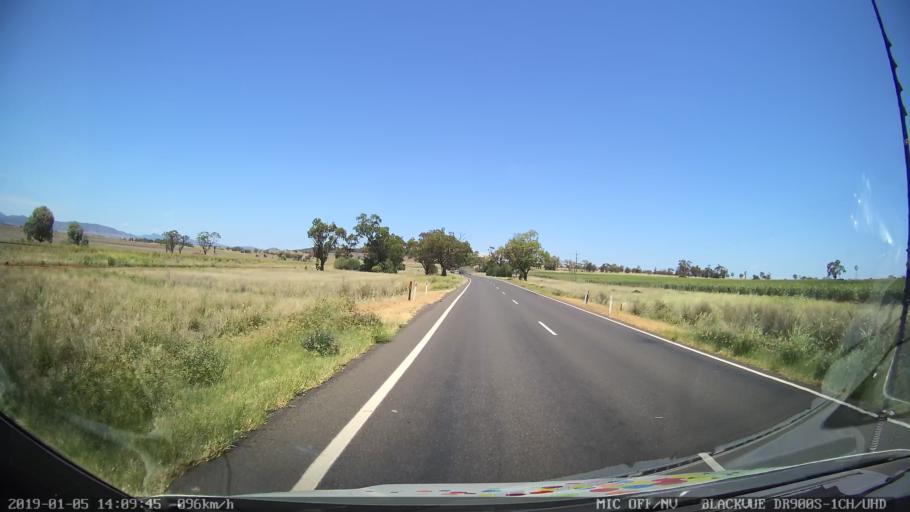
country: AU
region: New South Wales
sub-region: Gunnedah
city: Gunnedah
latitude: -31.2451
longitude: 150.4315
